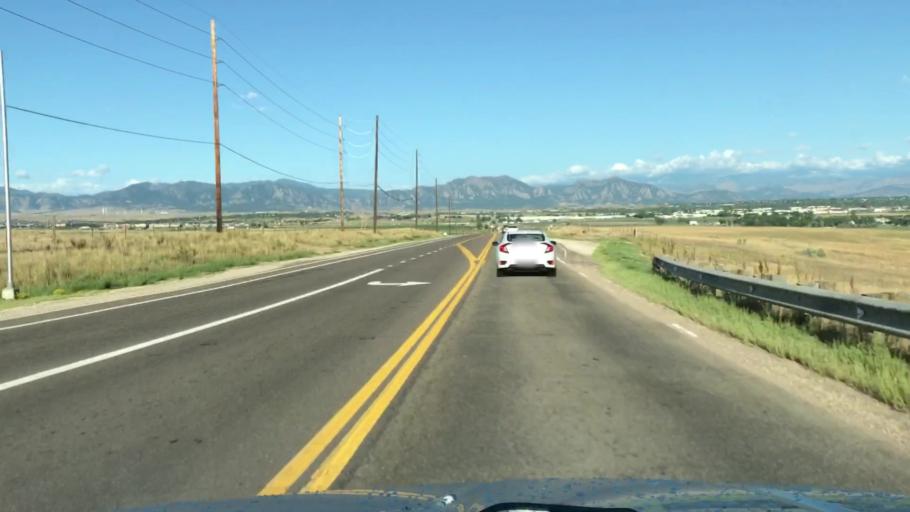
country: US
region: Colorado
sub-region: Broomfield County
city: Broomfield
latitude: 39.9564
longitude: -105.0718
